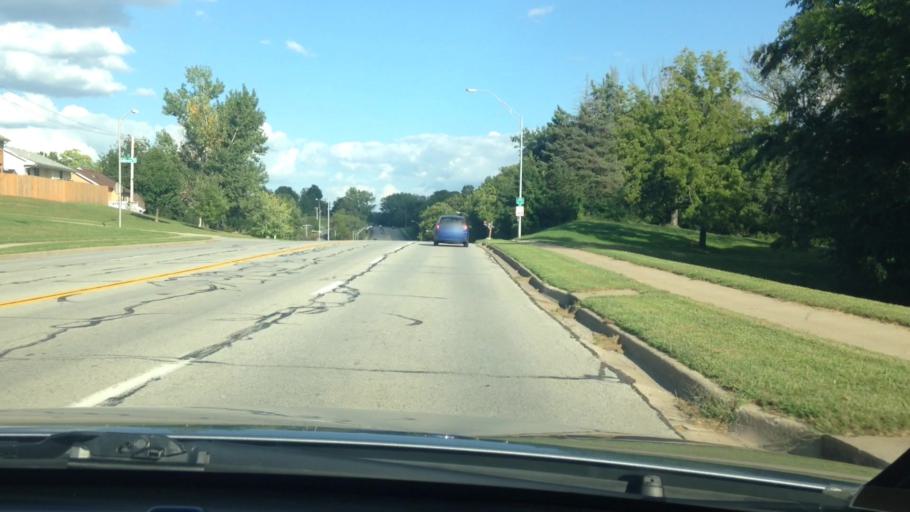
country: US
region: Missouri
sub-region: Clay County
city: Claycomo
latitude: 39.1805
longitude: -94.5078
